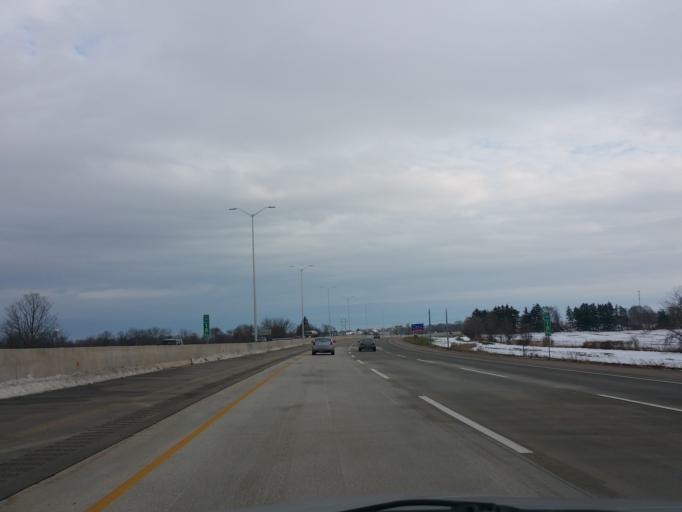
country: US
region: Illinois
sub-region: Winnebago County
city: Cherry Valley
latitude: 42.2471
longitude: -88.9357
